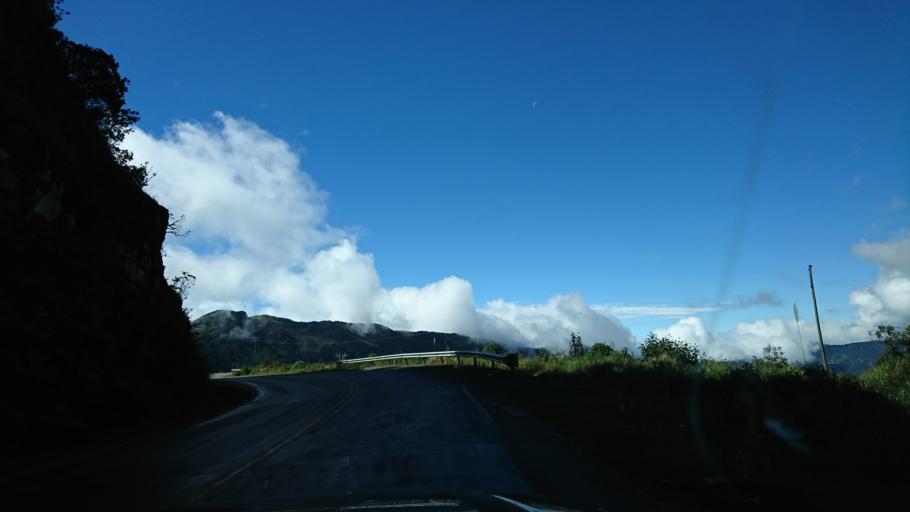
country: BO
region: La Paz
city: Coroico
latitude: -16.3037
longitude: -67.8959
